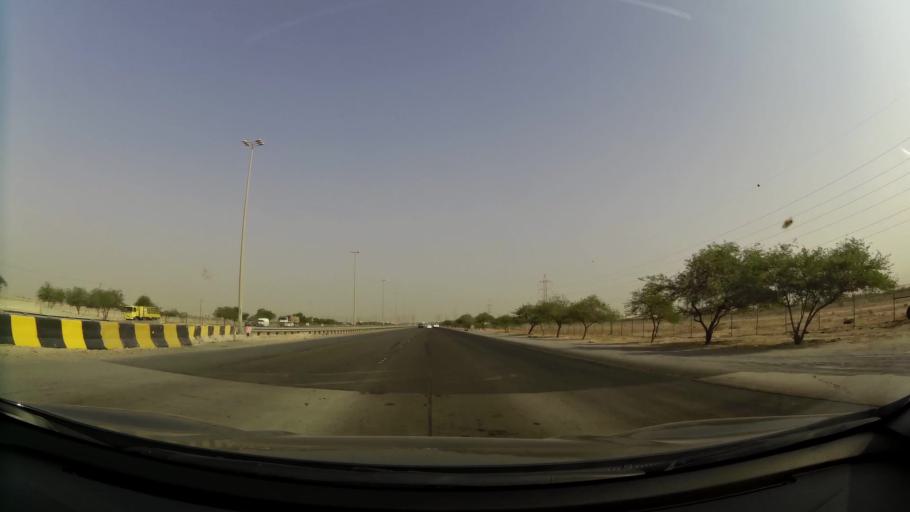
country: KW
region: Al Asimah
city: Ar Rabiyah
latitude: 29.2195
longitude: 47.8851
